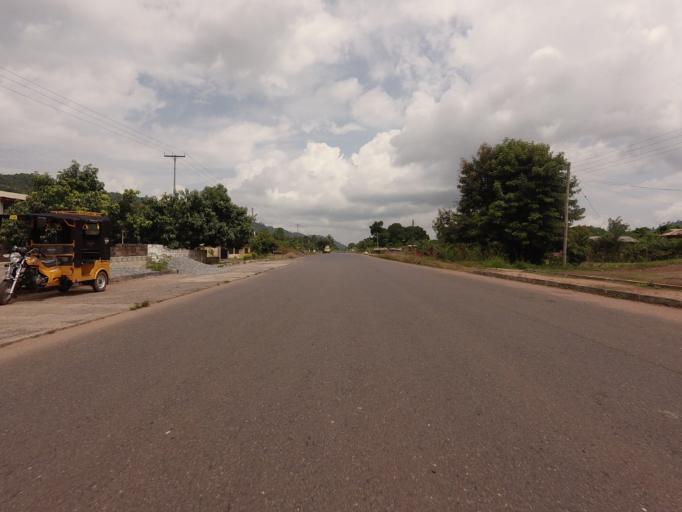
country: GH
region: Volta
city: Ho
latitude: 6.4998
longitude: 0.2049
